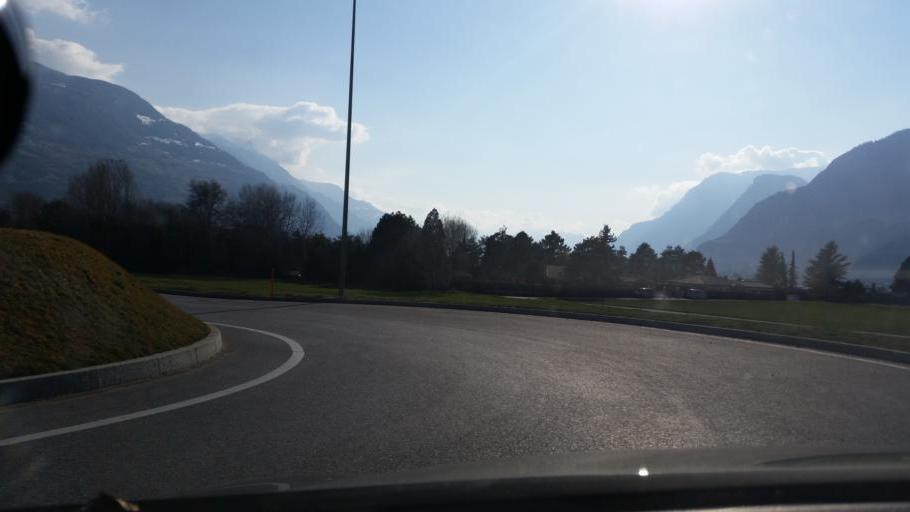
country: CH
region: Valais
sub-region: Conthey District
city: Vetroz
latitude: 46.2208
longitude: 7.2921
